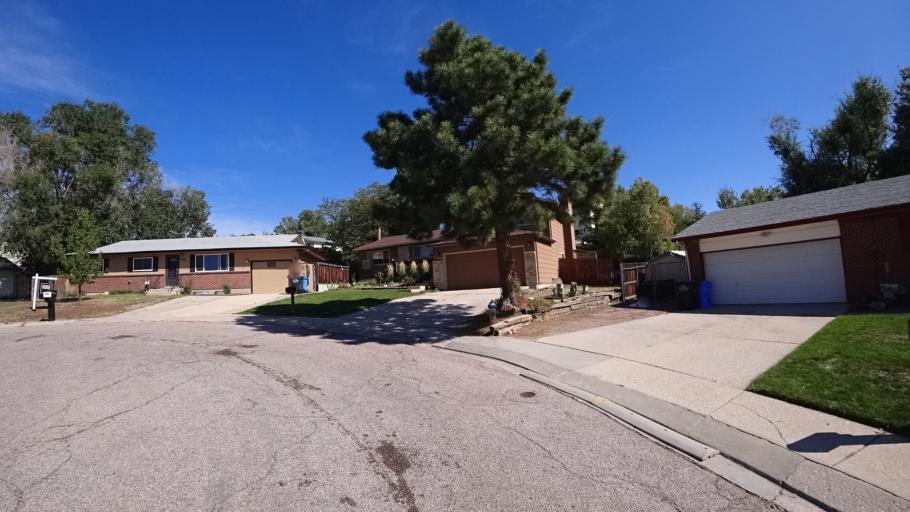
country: US
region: Colorado
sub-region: El Paso County
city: Colorado Springs
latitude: 38.9100
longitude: -104.7817
